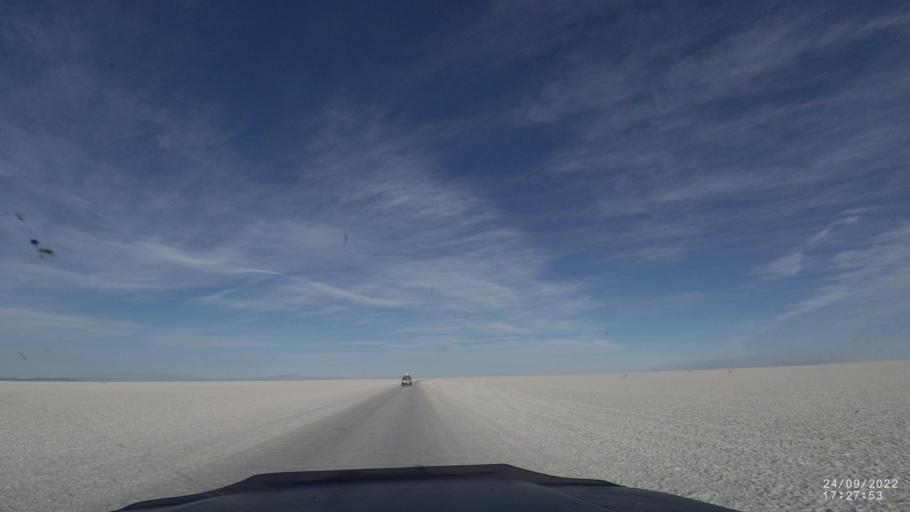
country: BO
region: Potosi
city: Colchani
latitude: -20.3013
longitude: -67.4390
